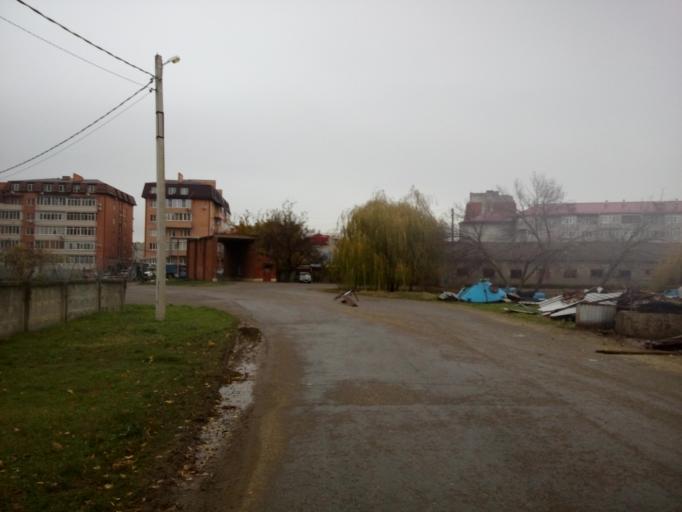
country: RU
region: Krasnodarskiy
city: Krasnodar
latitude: 45.0388
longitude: 39.0175
